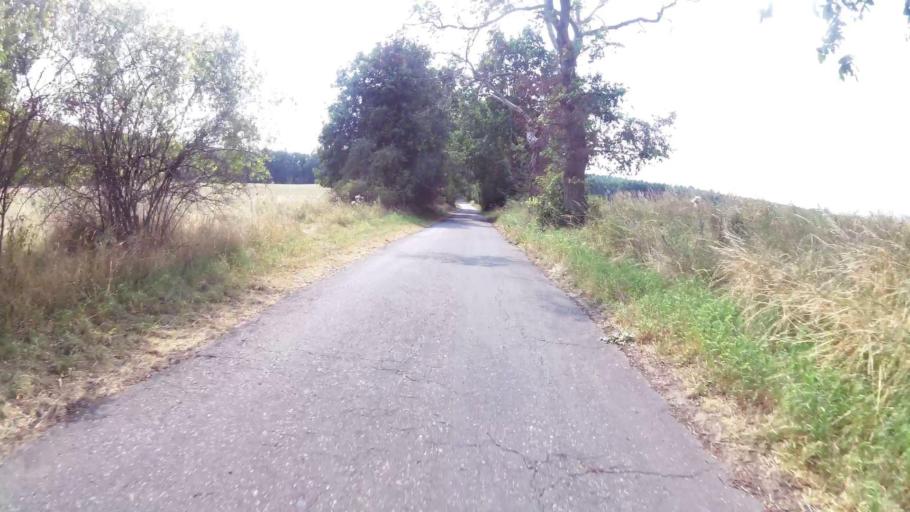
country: PL
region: West Pomeranian Voivodeship
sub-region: Powiat gryfinski
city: Mieszkowice
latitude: 52.8764
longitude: 14.5269
